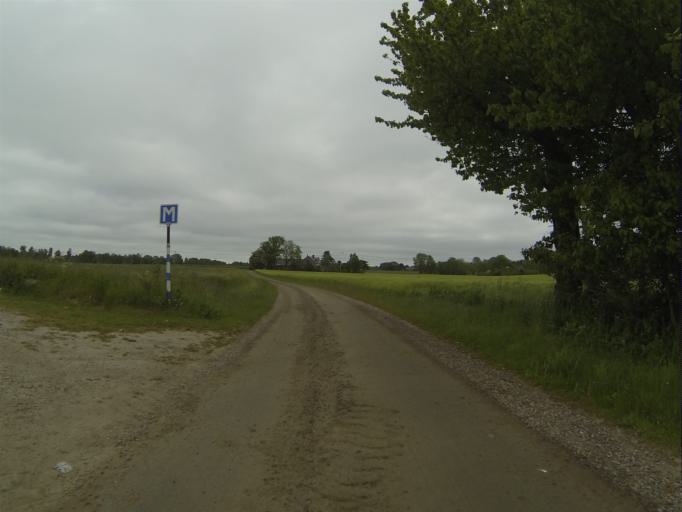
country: SE
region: Skane
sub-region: Staffanstorps Kommun
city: Staffanstorp
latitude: 55.6895
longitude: 13.3097
